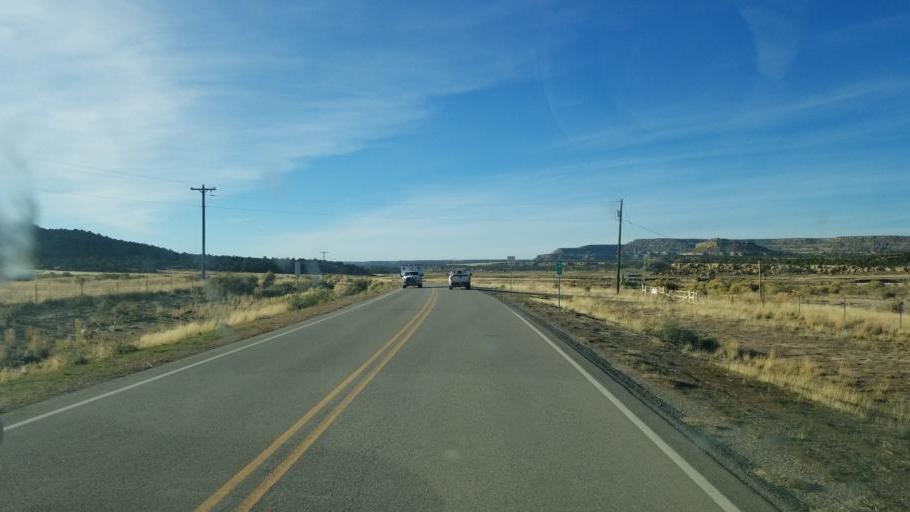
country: US
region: New Mexico
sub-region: San Juan County
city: Bloomfield
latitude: 36.7370
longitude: -107.5708
